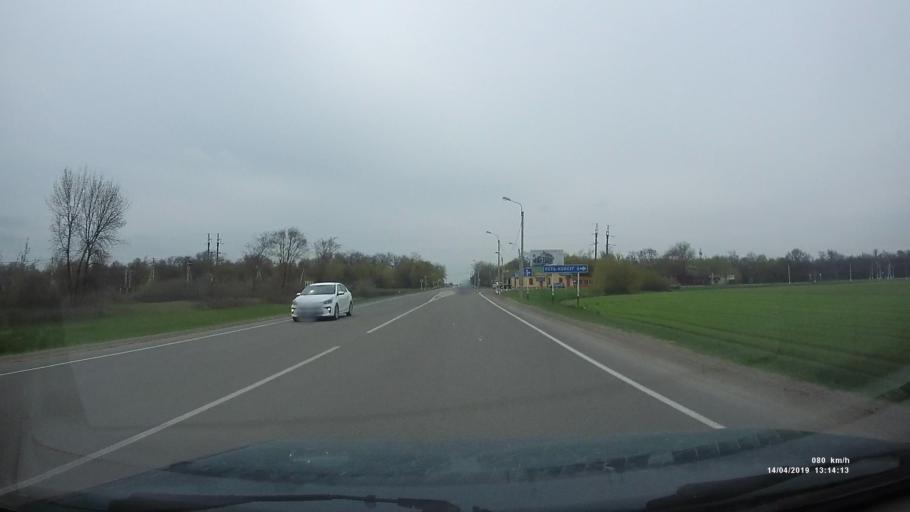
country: RU
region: Rostov
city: Kuleshovka
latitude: 47.0920
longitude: 39.6127
